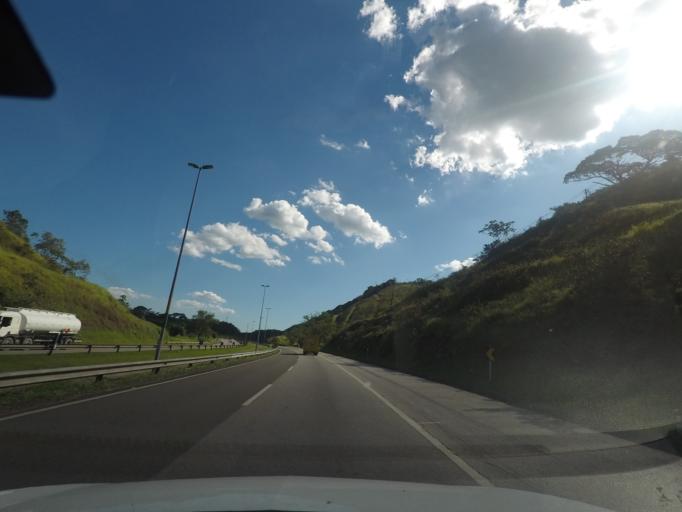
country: BR
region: Rio de Janeiro
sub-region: Guapimirim
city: Guapimirim
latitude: -22.5744
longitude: -43.0093
